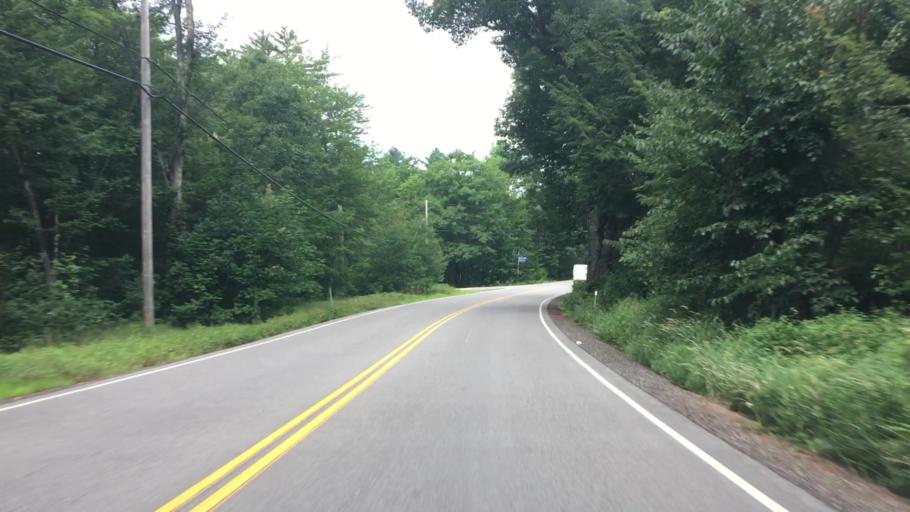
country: US
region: New Hampshire
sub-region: Belknap County
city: Laconia
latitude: 43.5791
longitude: -71.5102
